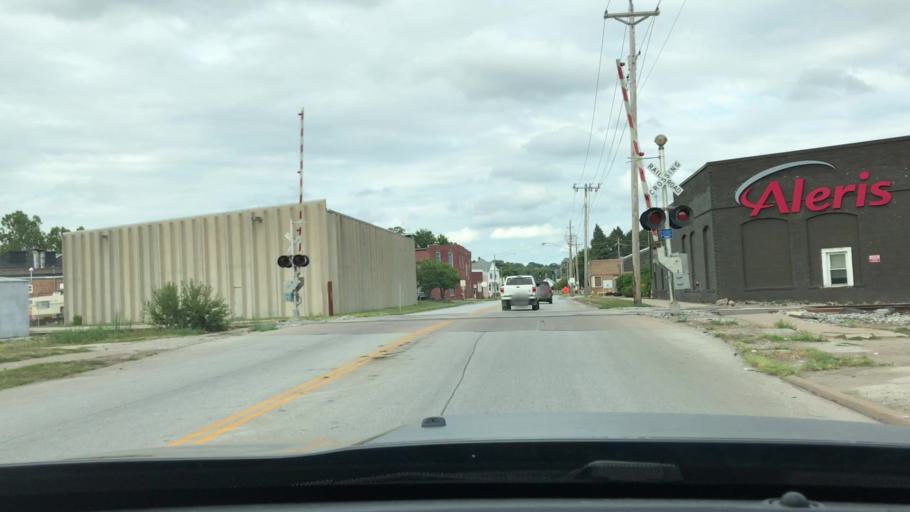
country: US
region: Iowa
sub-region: Scott County
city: Davenport
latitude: 41.5186
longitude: -90.6034
